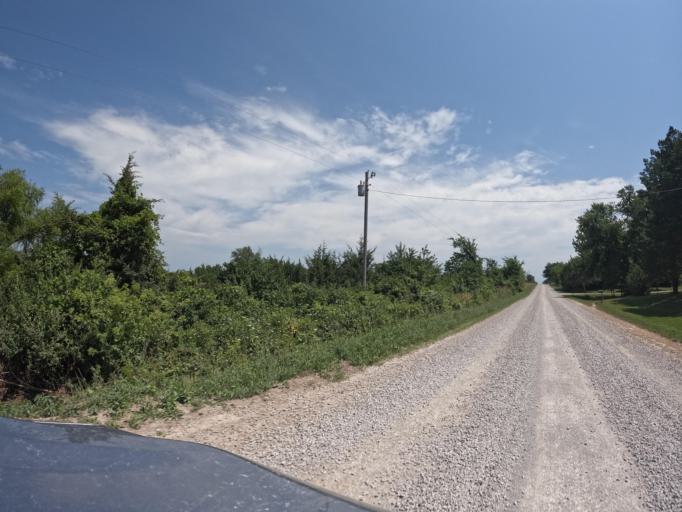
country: US
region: Iowa
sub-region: Appanoose County
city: Centerville
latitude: 40.7867
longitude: -92.9315
